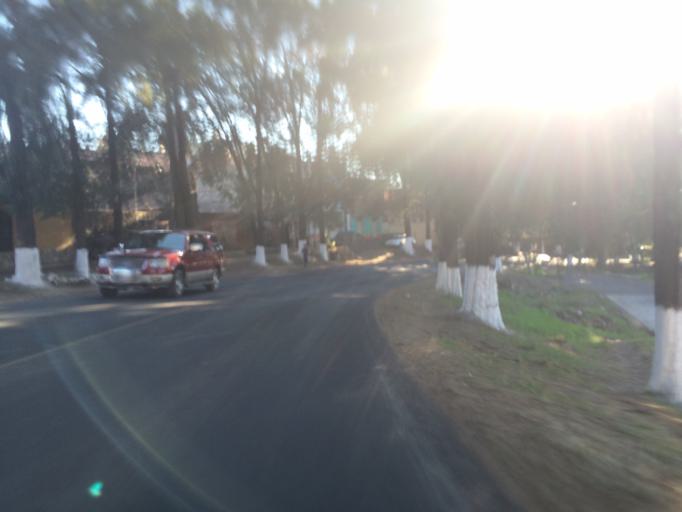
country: MX
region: Michoacan
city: Patzcuaro
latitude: 19.5058
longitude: -101.6124
